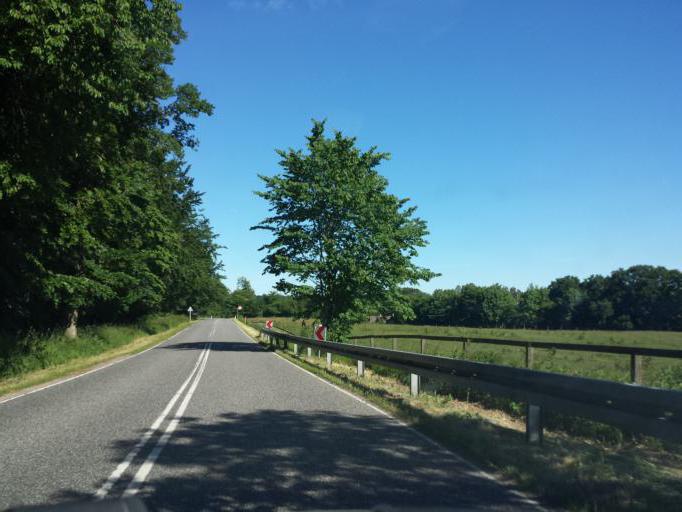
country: DK
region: Capital Region
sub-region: Egedal Kommune
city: Ganlose
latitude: 55.8147
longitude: 12.2606
